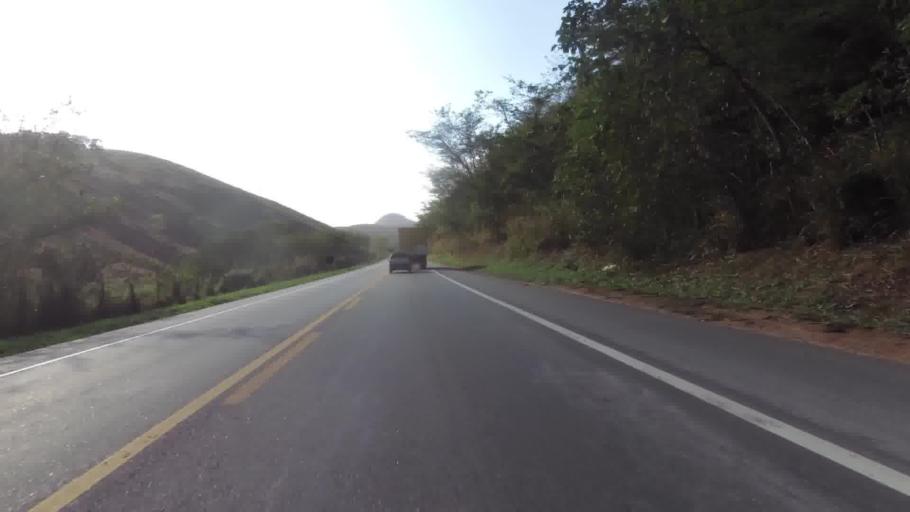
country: BR
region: Espirito Santo
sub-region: Mimoso Do Sul
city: Mimoso do Sul
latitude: -21.1843
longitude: -41.2943
